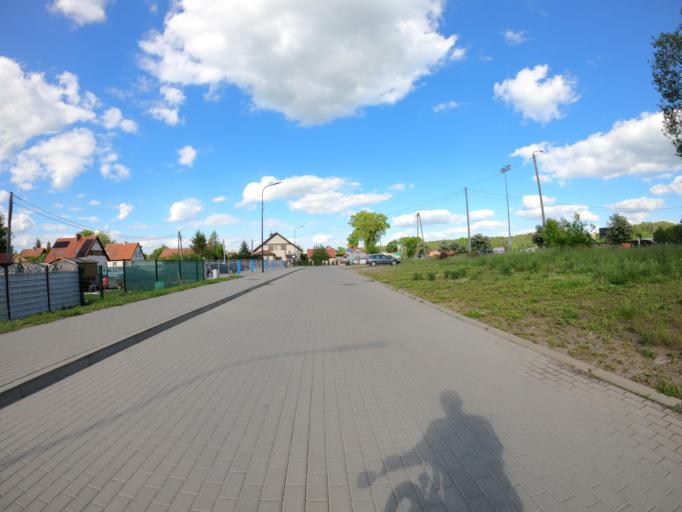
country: PL
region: Warmian-Masurian Voivodeship
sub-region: Powiat lidzbarski
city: Lidzbark Warminski
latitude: 54.1277
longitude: 20.5970
